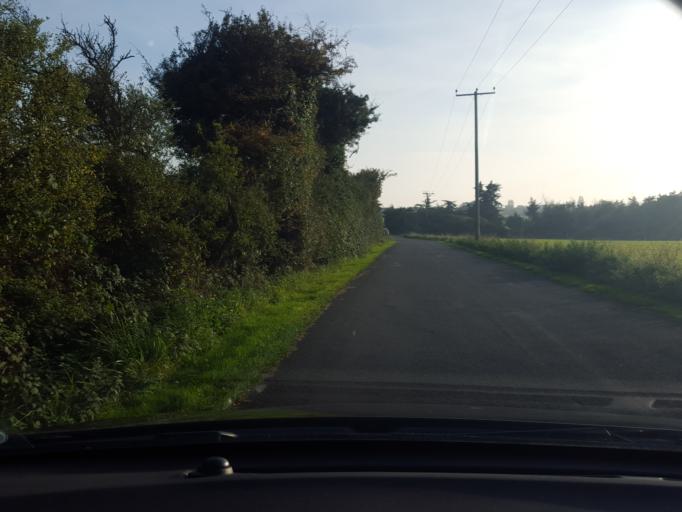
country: GB
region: England
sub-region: Essex
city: Walton-on-the-Naze
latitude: 51.8597
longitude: 1.2589
